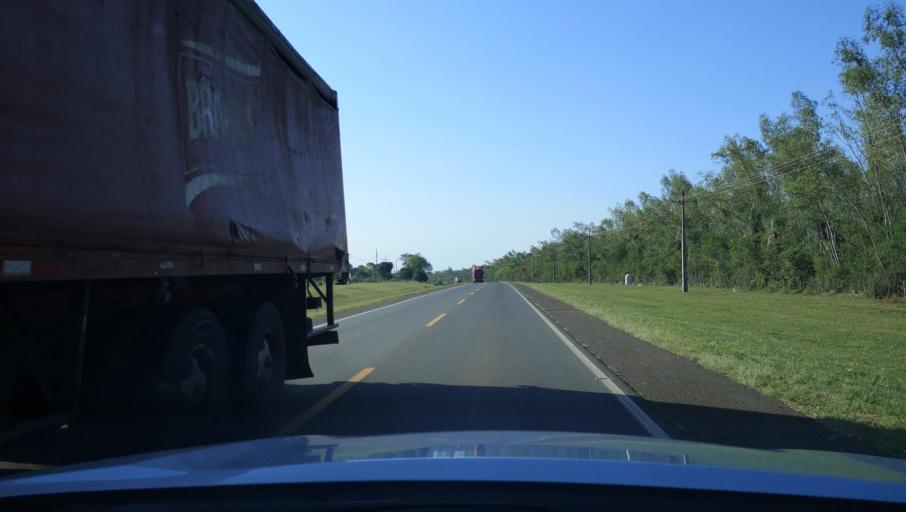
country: PY
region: Misiones
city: Santa Maria
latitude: -26.7631
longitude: -57.0330
